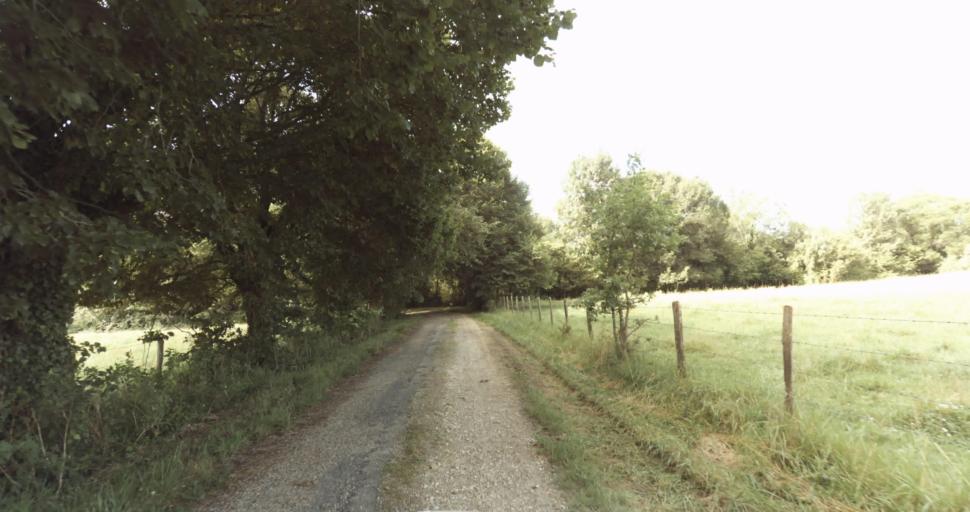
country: FR
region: Aquitaine
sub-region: Departement de la Gironde
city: Bazas
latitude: 44.4368
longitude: -0.1847
